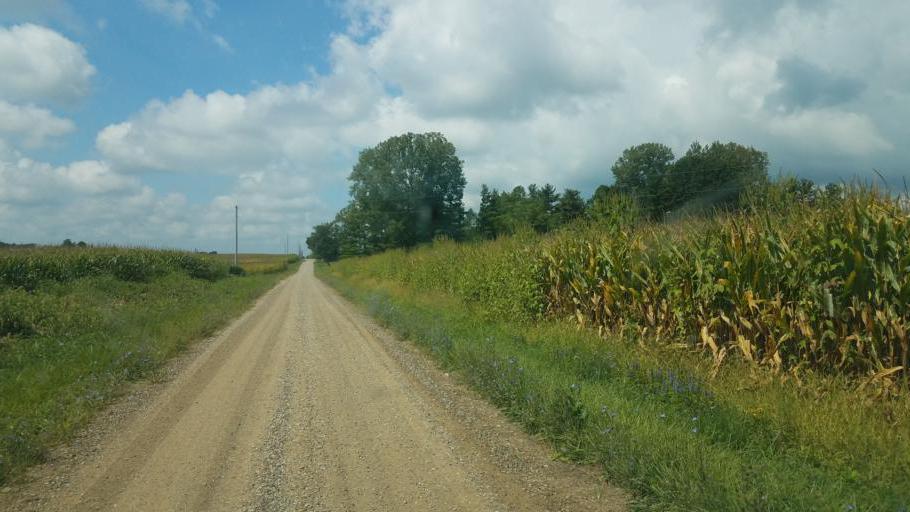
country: US
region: Ohio
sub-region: Licking County
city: Utica
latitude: 40.2664
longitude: -82.4571
